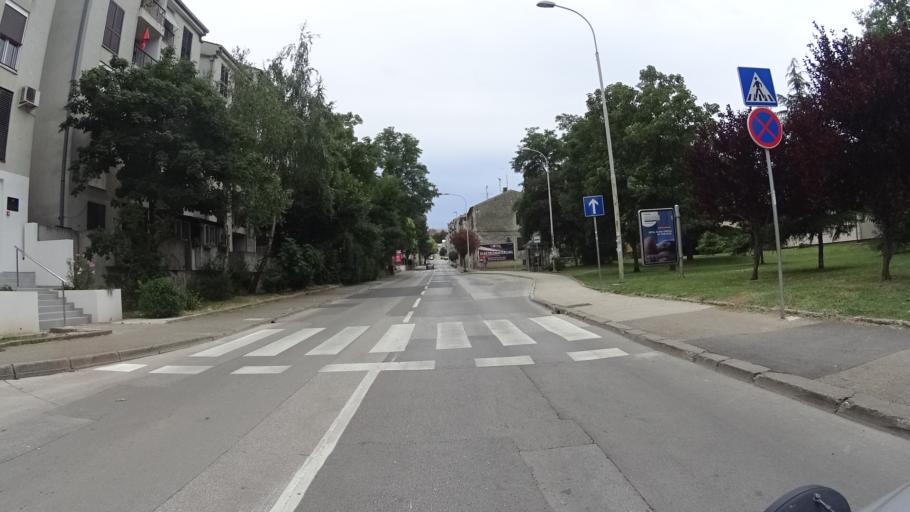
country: HR
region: Istarska
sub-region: Grad Pula
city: Pula
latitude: 44.8630
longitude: 13.8486
